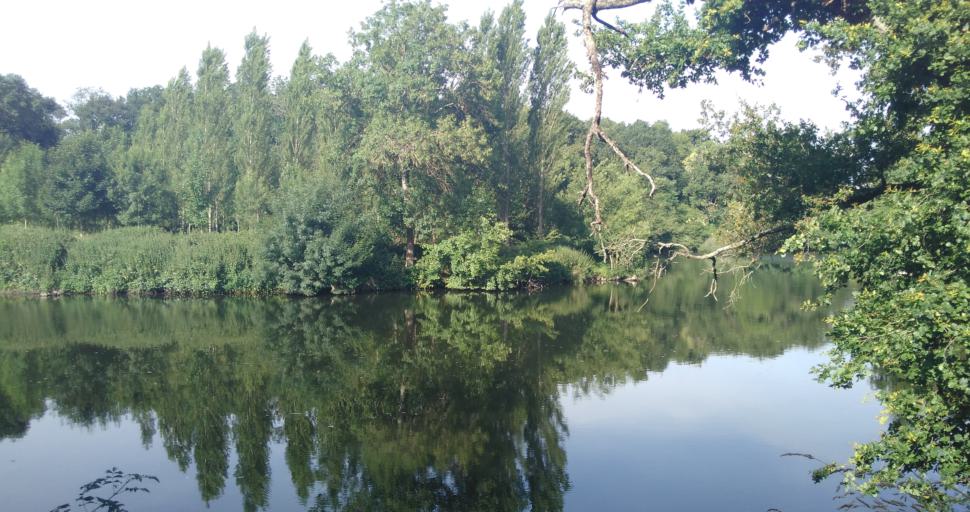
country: FR
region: Pays de la Loire
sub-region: Departement de la Loire-Atlantique
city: Clisson
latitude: 47.0980
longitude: -1.2871
